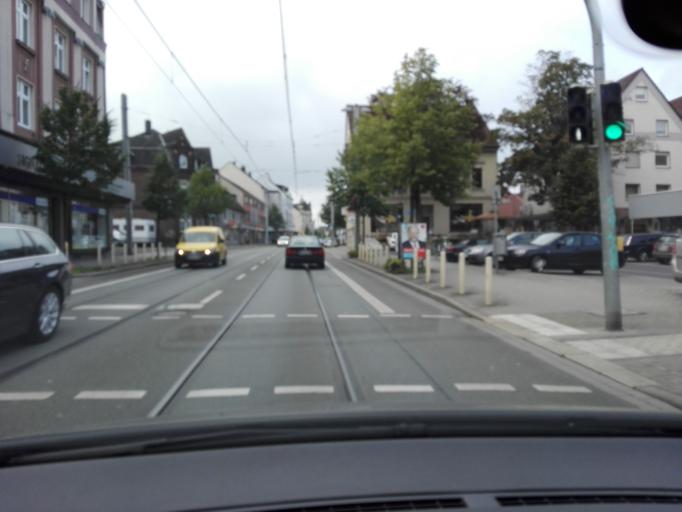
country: DE
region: North Rhine-Westphalia
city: Lanstrop
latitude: 51.5281
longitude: 7.5846
